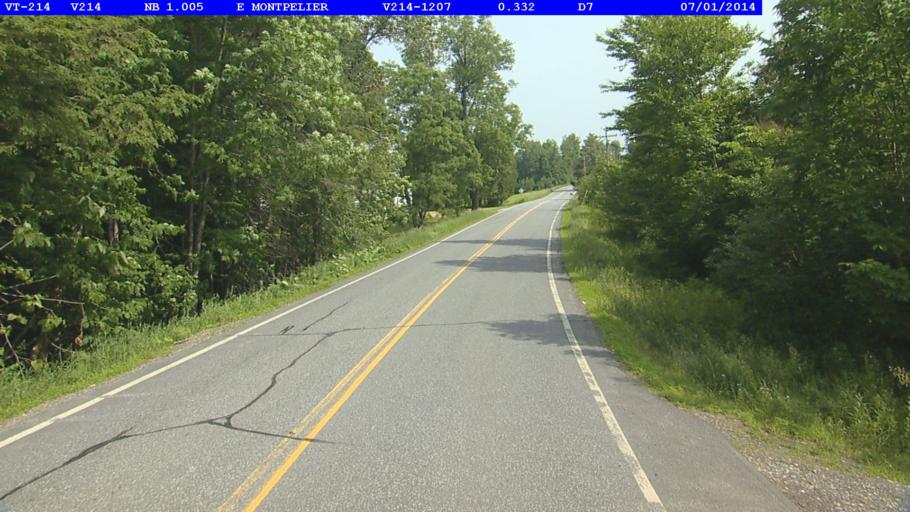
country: US
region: Vermont
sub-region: Washington County
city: Barre
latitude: 44.2901
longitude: -72.4444
